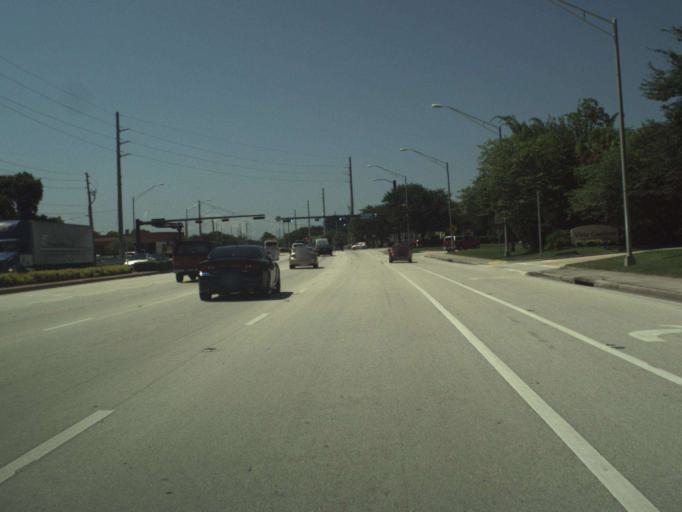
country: US
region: Florida
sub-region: Indian River County
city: Florida Ridge
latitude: 27.6075
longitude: -80.3831
